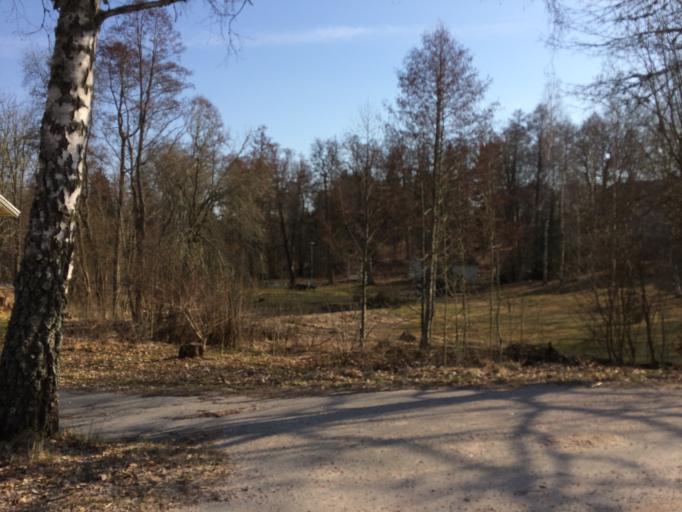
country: SE
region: Soedermanland
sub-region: Katrineholms Kommun
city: Katrineholm
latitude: 59.0900
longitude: 16.2160
